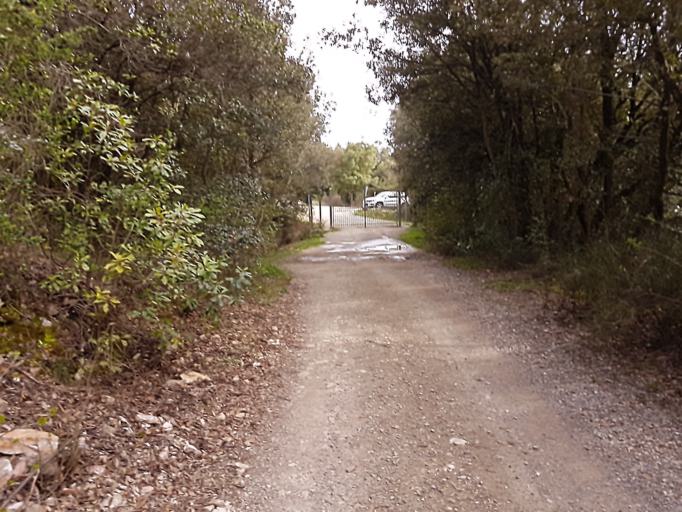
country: IT
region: Umbria
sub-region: Provincia di Perugia
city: Corciano
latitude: 43.1326
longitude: 12.2993
